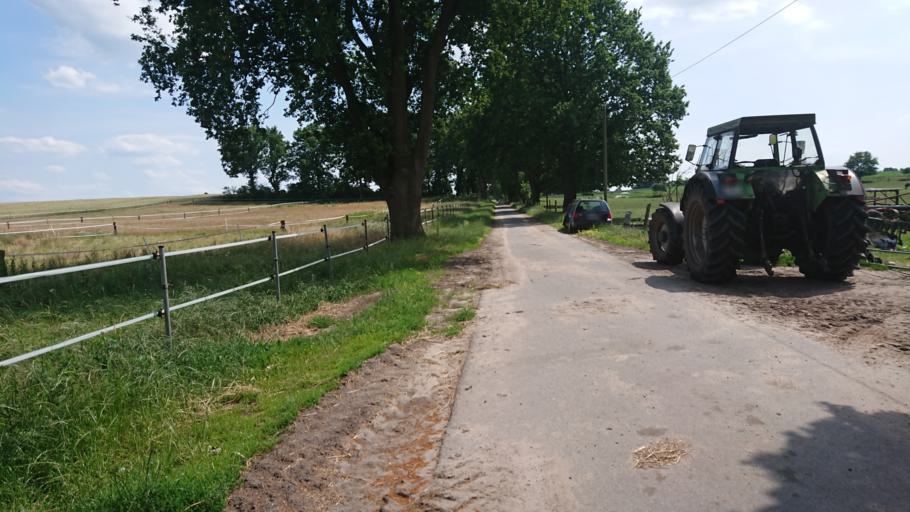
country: DE
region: Lower Saxony
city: Husum
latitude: 52.5448
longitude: 9.2106
